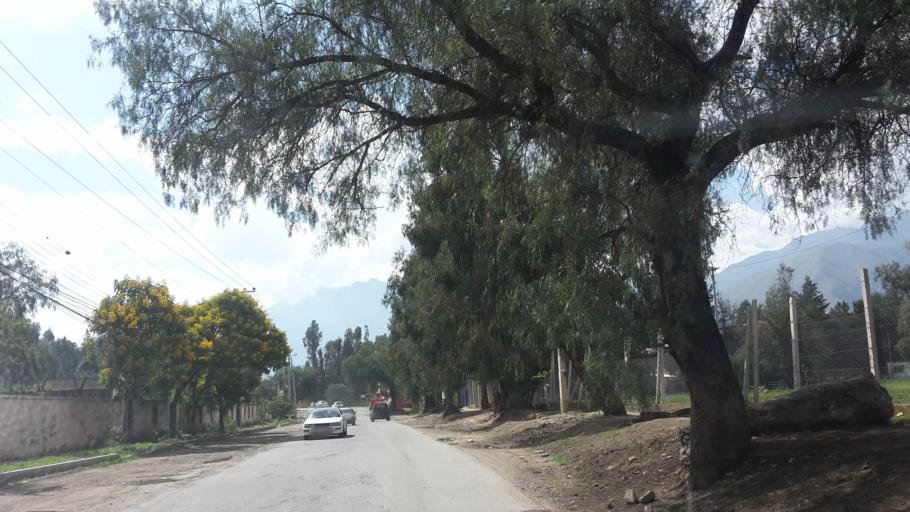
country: BO
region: Cochabamba
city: Cochabamba
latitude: -17.3370
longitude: -66.2278
